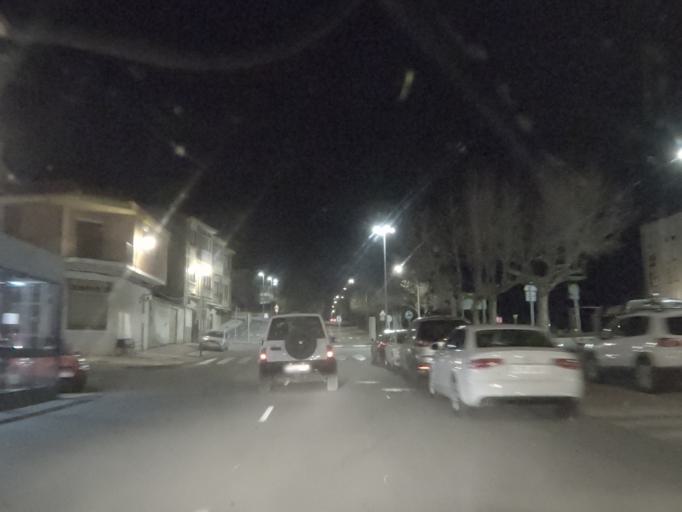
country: ES
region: Castille and Leon
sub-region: Provincia de Zamora
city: Benavente
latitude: 42.0071
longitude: -5.6842
